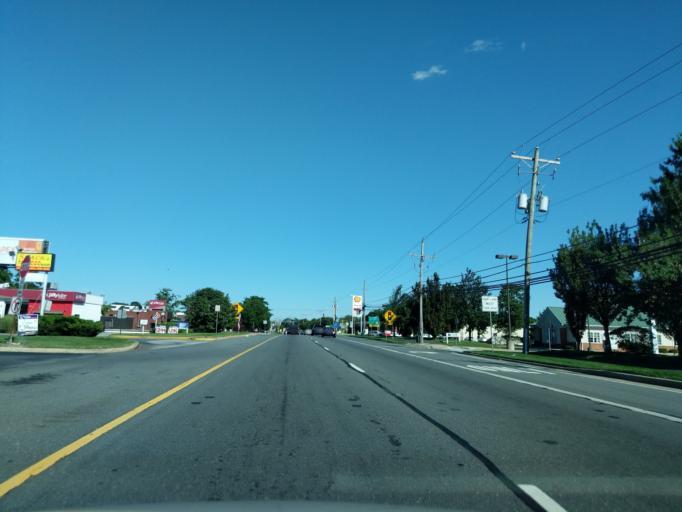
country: US
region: Delaware
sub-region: New Castle County
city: Glasgow
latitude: 39.6045
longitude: -75.7482
